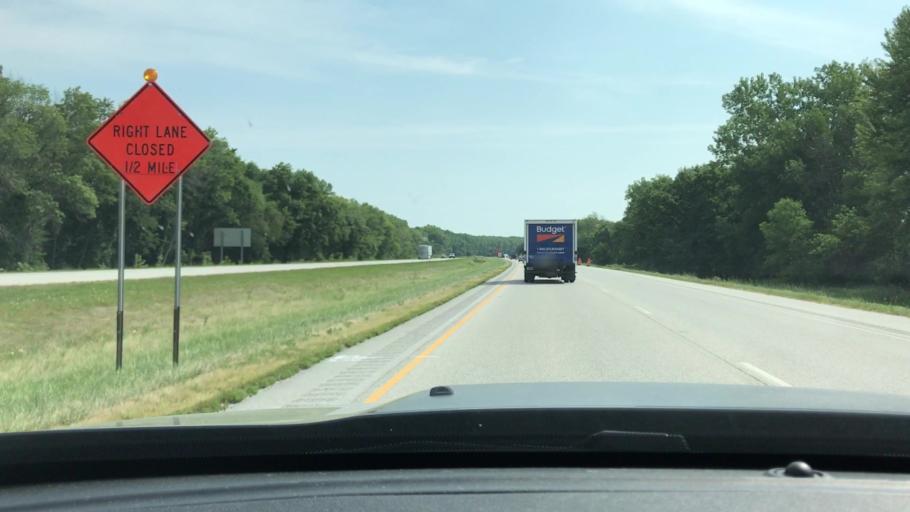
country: US
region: Illinois
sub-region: Rock Island County
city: Carbon Cliff
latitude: 41.4582
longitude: -90.4056
